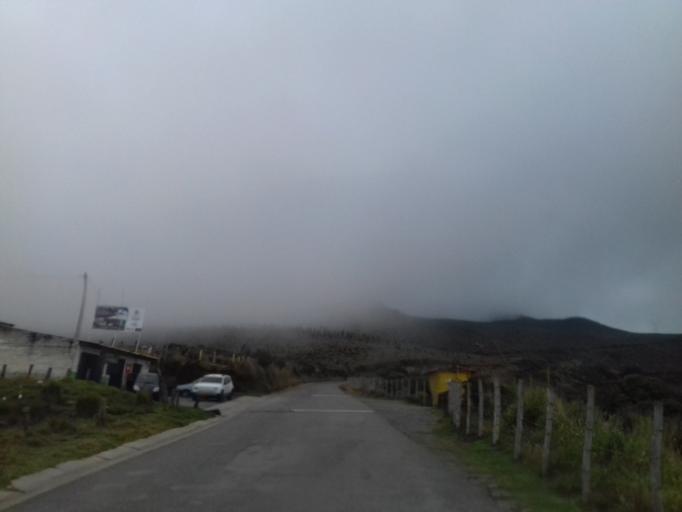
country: CO
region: Caldas
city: Villamaria
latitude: 4.9807
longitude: -75.3353
